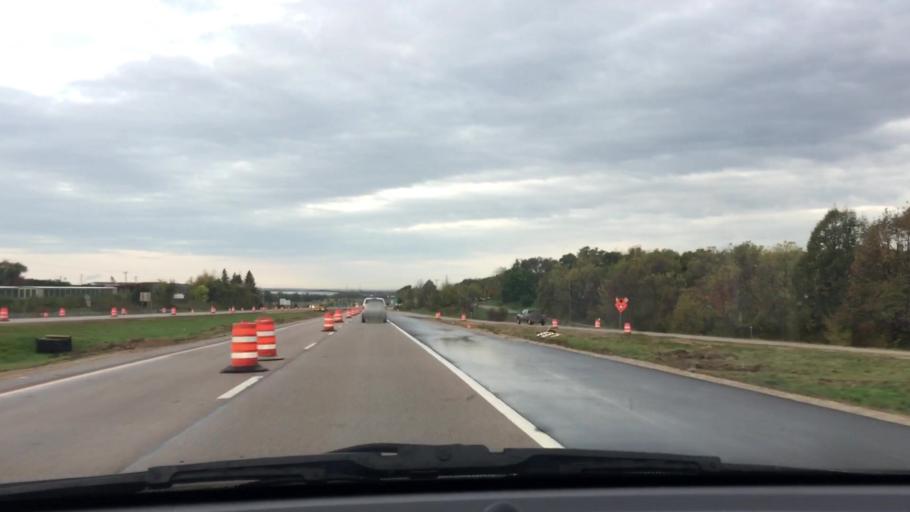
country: US
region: Wisconsin
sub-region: Rock County
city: Beloit
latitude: 42.5392
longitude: -88.9508
